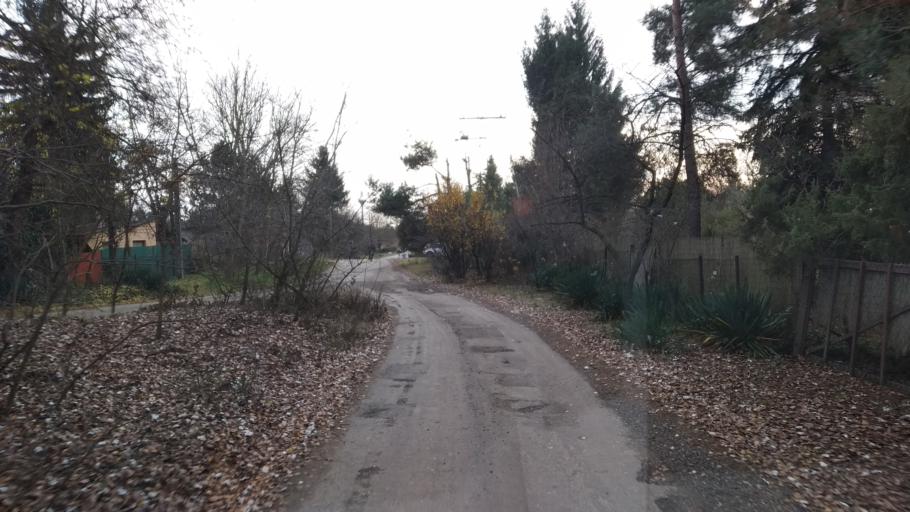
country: HU
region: Pest
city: God
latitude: 47.6761
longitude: 19.1112
